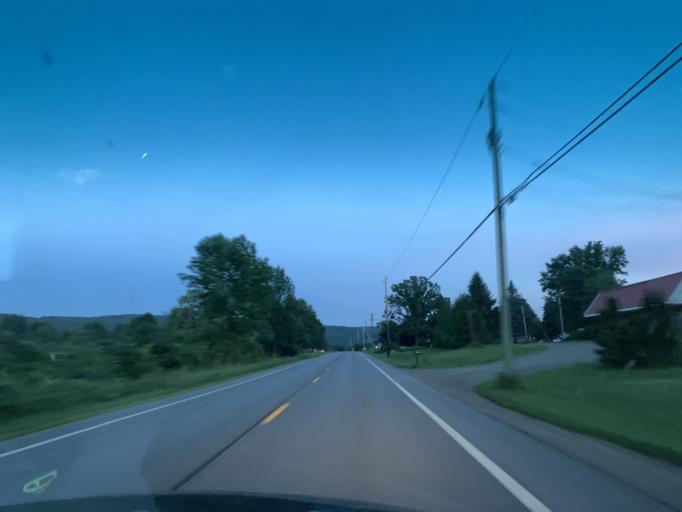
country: US
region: New York
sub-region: Chenango County
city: New Berlin
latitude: 42.5925
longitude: -75.3372
